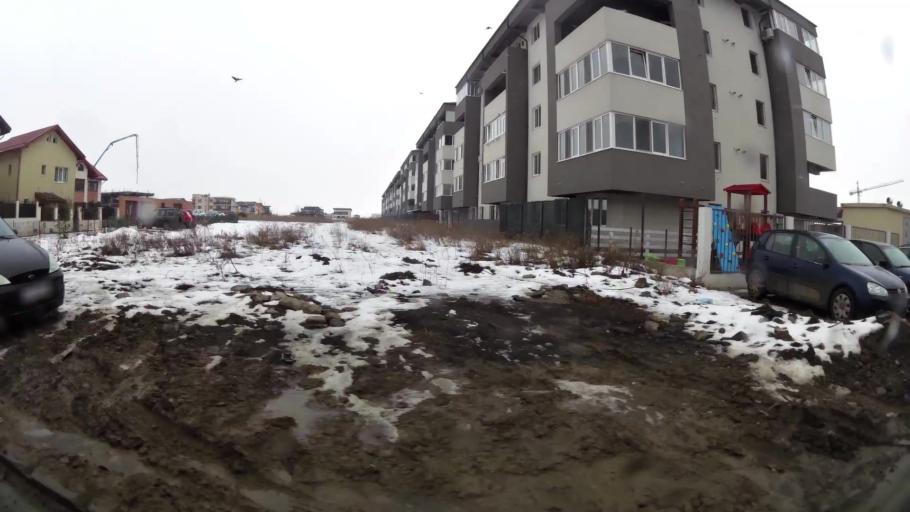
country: RO
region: Ilfov
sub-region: Comuna Glina
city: Catelu
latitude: 44.4180
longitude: 26.1910
